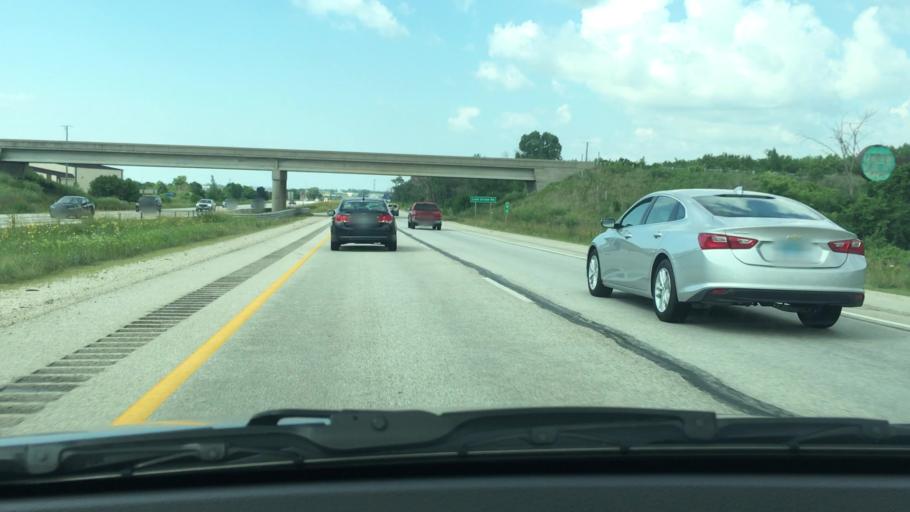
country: US
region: Wisconsin
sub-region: Fond du Lac County
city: Fond du Lac
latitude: 43.7105
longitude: -88.4422
